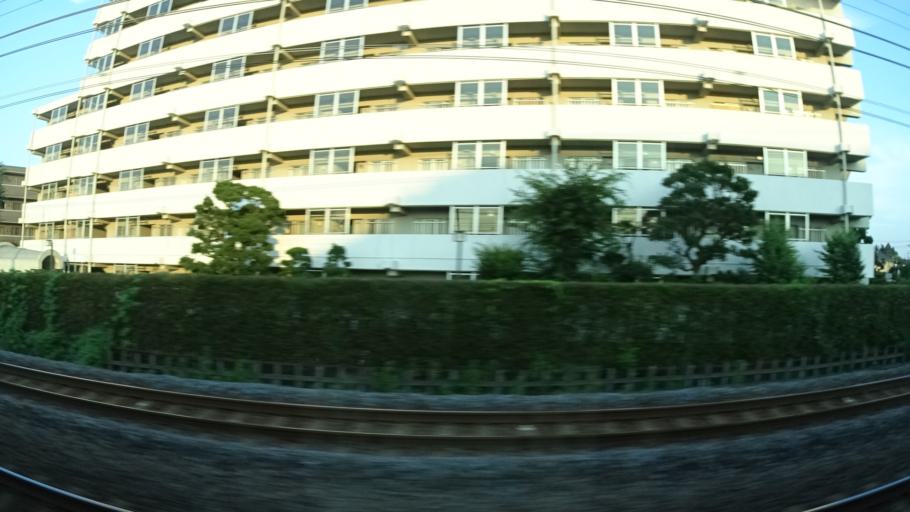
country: JP
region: Chiba
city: Kashiwa
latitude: 35.8534
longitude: 139.9640
